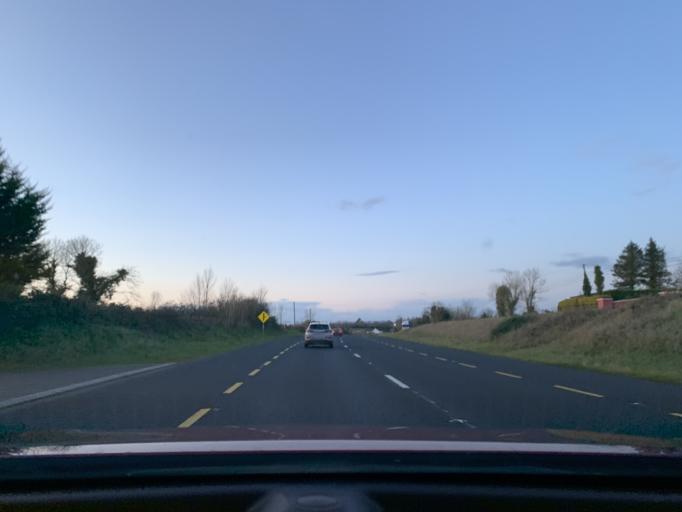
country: IE
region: Connaught
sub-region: County Leitrim
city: Carrick-on-Shannon
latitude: 53.8852
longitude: -7.9411
